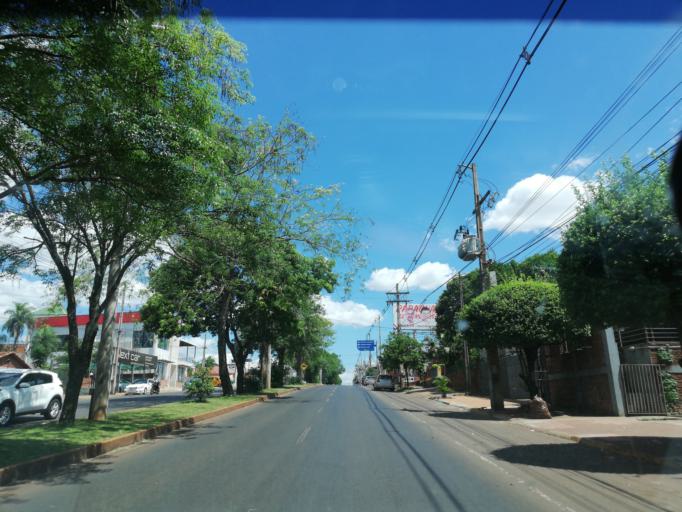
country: PY
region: Itapua
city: Encarnacion
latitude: -27.3392
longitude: -55.8581
